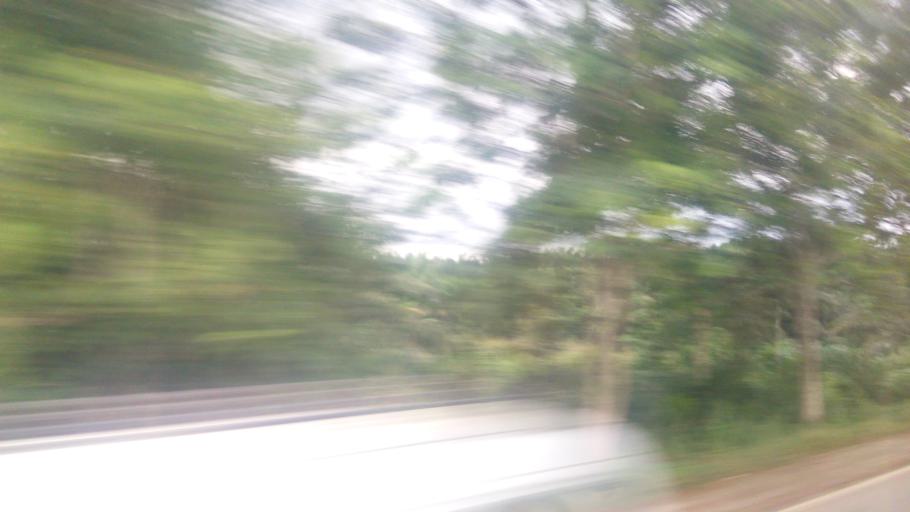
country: GH
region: Western
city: Takoradi
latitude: 4.8973
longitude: -1.9319
